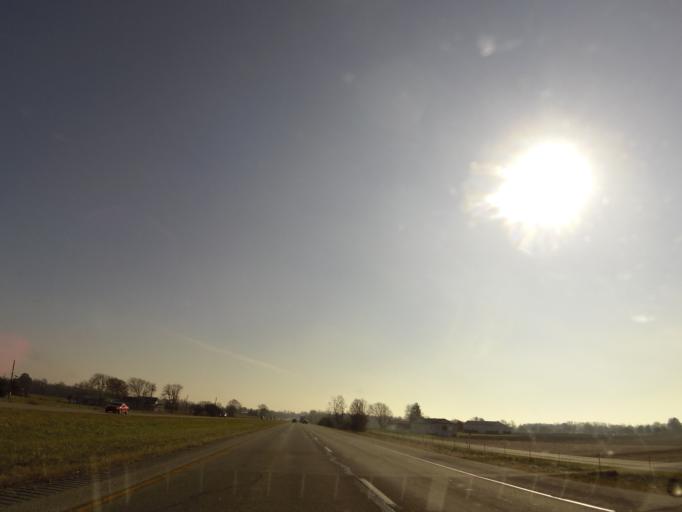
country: US
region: Indiana
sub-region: Hancock County
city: New Palestine
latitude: 39.6188
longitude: -85.8707
